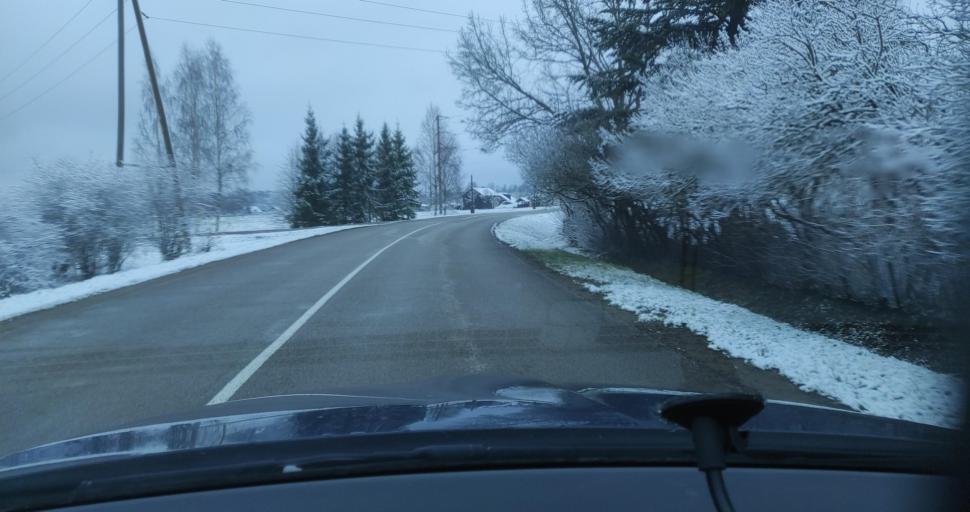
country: LV
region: Skrunda
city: Skrunda
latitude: 56.8664
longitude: 22.2320
